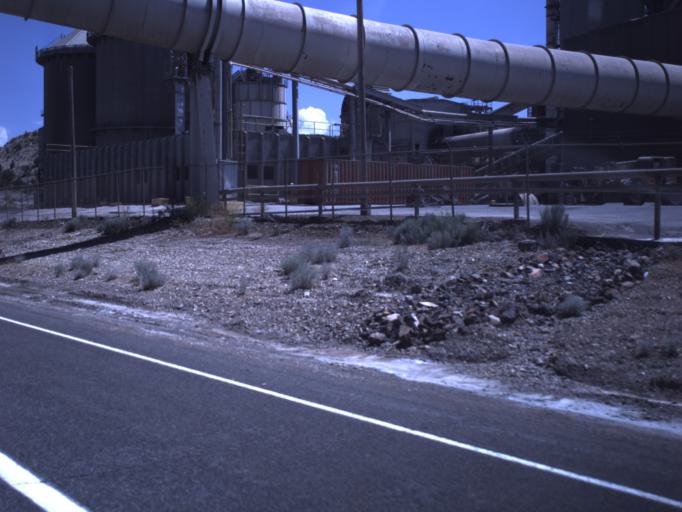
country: US
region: Utah
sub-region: Juab County
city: Nephi
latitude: 39.5639
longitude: -112.1986
